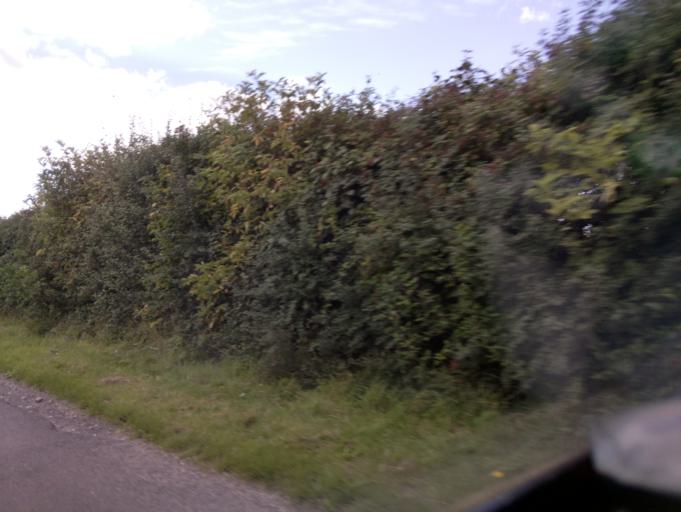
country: GB
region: England
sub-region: Wiltshire
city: Salisbury
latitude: 51.0969
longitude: -1.7485
